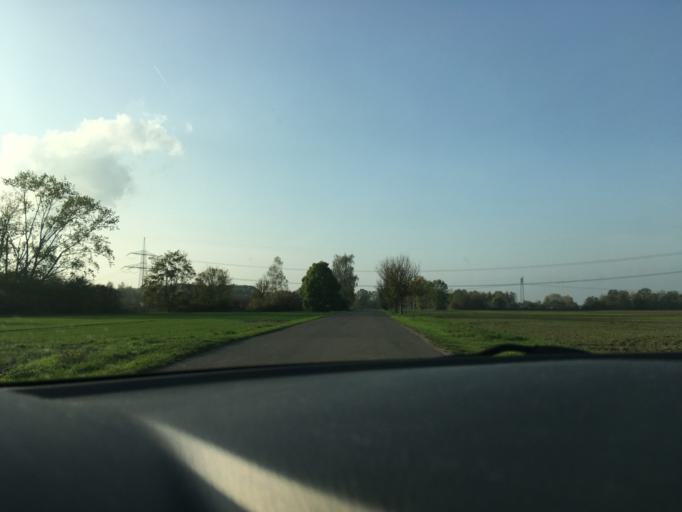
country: DE
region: Saxony
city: Neukieritzsch
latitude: 51.1848
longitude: 12.4318
